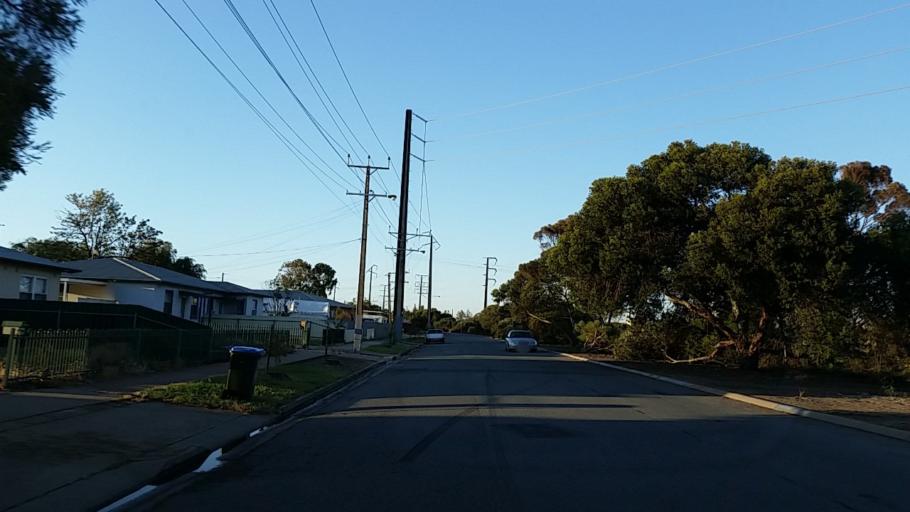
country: AU
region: South Australia
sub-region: Port Adelaide Enfield
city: Birkenhead
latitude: -34.8068
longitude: 138.5064
